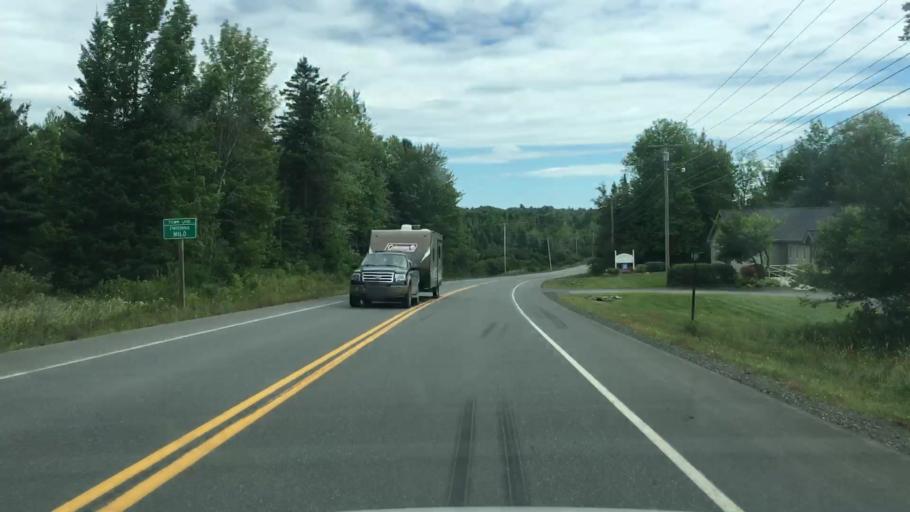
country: US
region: Maine
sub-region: Piscataquis County
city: Milo
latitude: 45.2415
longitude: -69.0375
